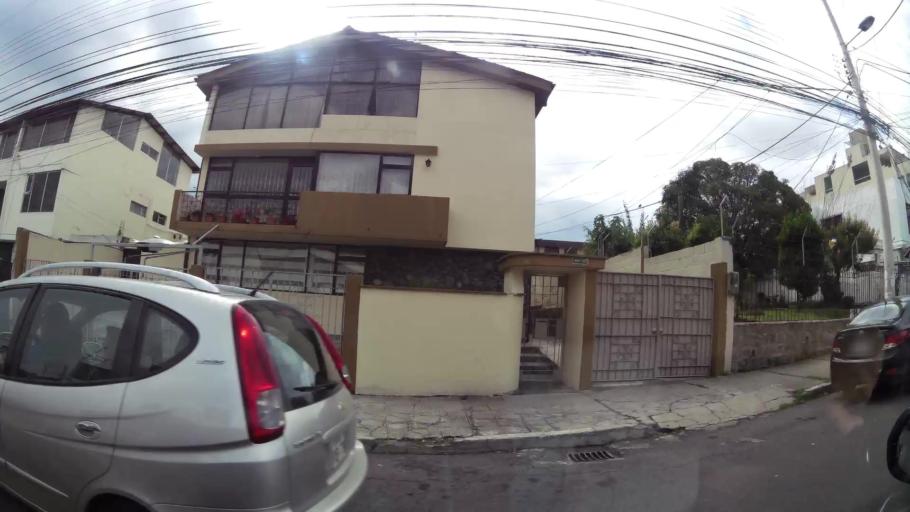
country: EC
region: Pichincha
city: Quito
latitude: -0.1596
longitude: -78.4803
